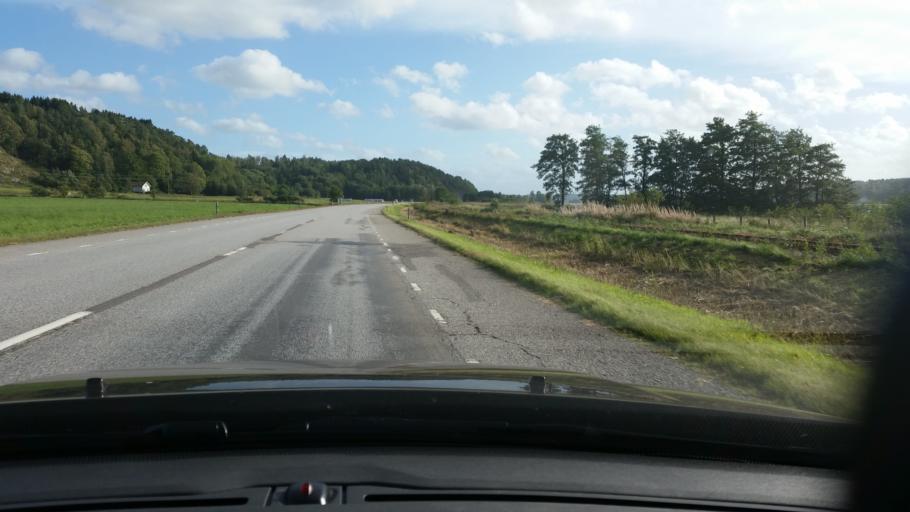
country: SE
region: Vaestra Goetaland
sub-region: Lilla Edets Kommun
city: Lodose
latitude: 58.0510
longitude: 12.1491
